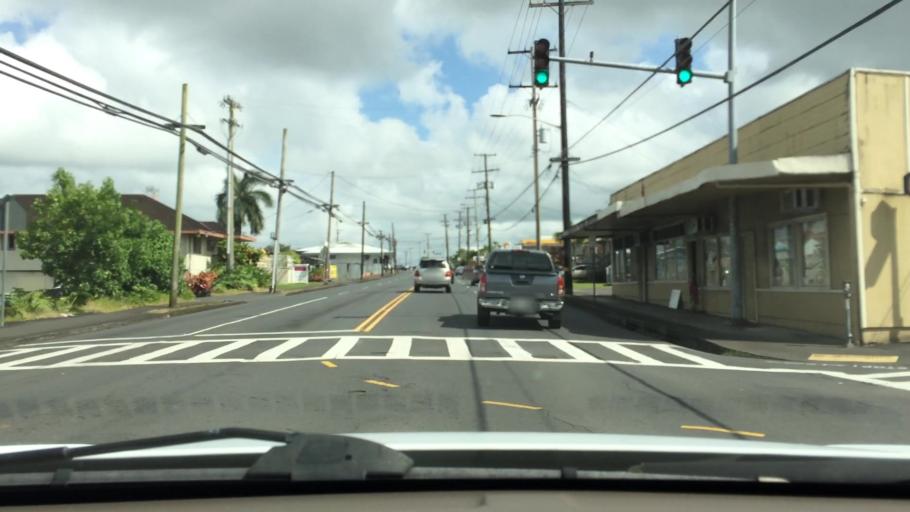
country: US
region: Hawaii
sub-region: Hawaii County
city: Hilo
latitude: 19.7136
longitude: -155.0775
